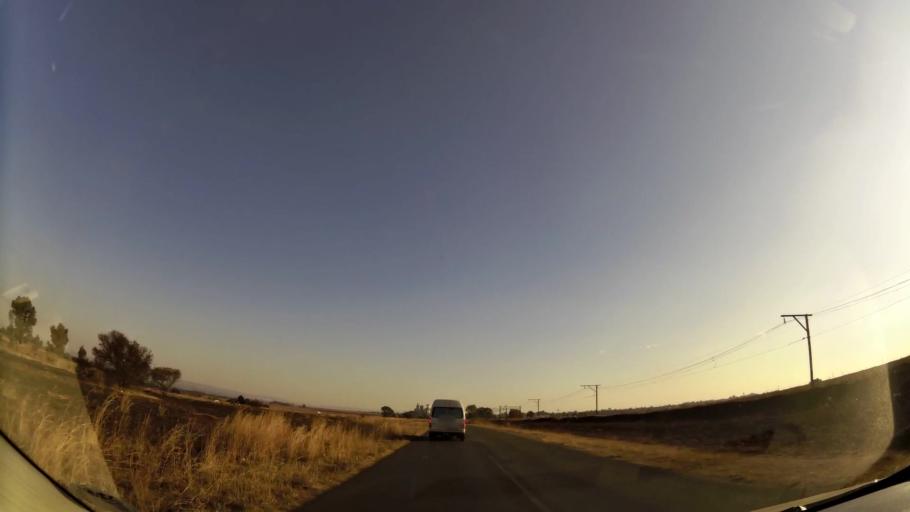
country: ZA
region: Gauteng
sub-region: West Rand District Municipality
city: Randfontein
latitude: -26.1990
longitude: 27.6759
